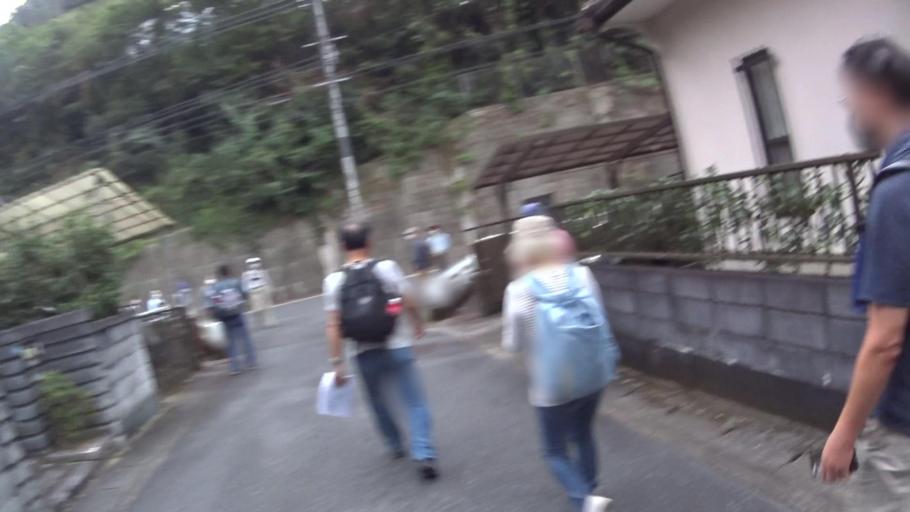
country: JP
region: Osaka
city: Kaizuka
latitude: 34.4592
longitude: 135.2917
